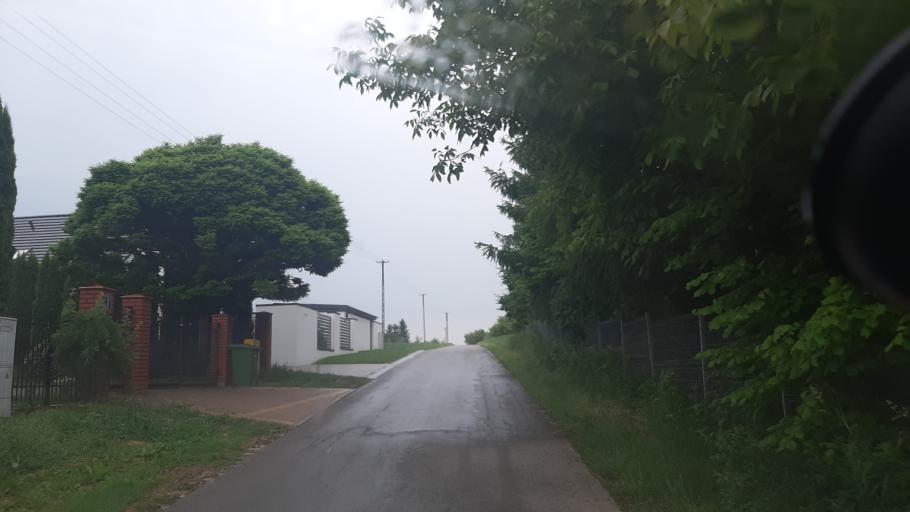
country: PL
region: Lublin Voivodeship
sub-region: Powiat lubelski
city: Garbow
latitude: 51.3534
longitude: 22.3465
